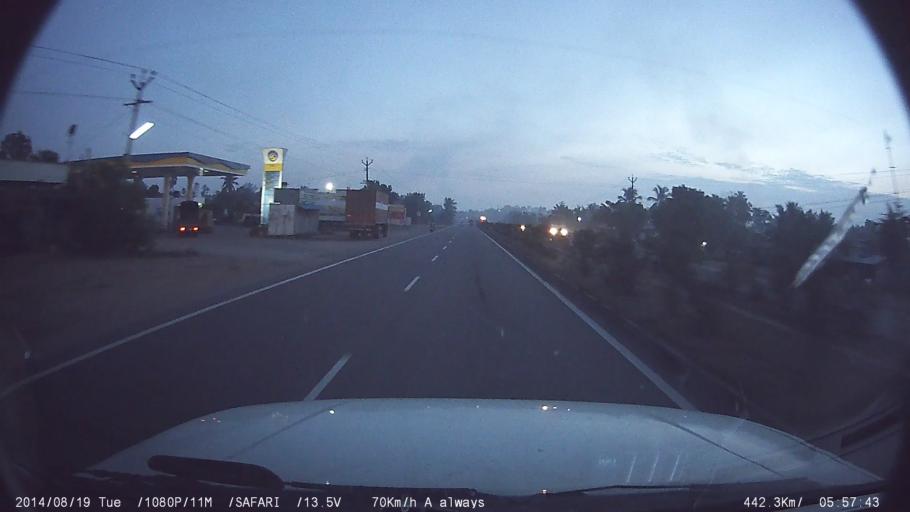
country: IN
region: Tamil Nadu
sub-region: Salem
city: Omalur
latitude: 11.7749
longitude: 78.0556
